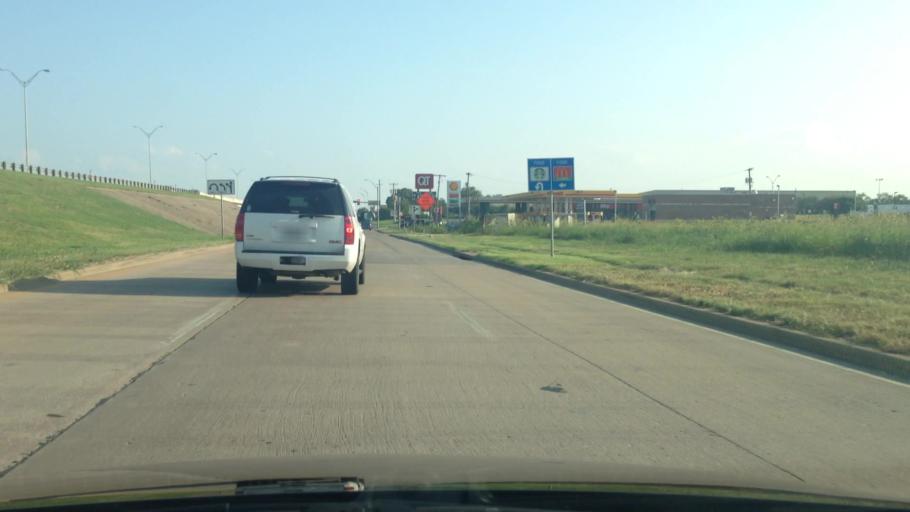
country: US
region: Texas
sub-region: Tarrant County
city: Everman
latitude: 32.6294
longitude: -97.3221
